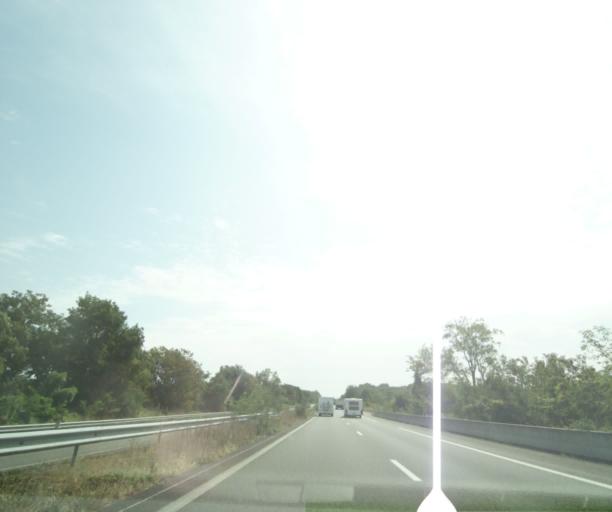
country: FR
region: Poitou-Charentes
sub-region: Departement de la Charente-Maritime
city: Saint-Savinien
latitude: 45.8675
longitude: -0.6222
